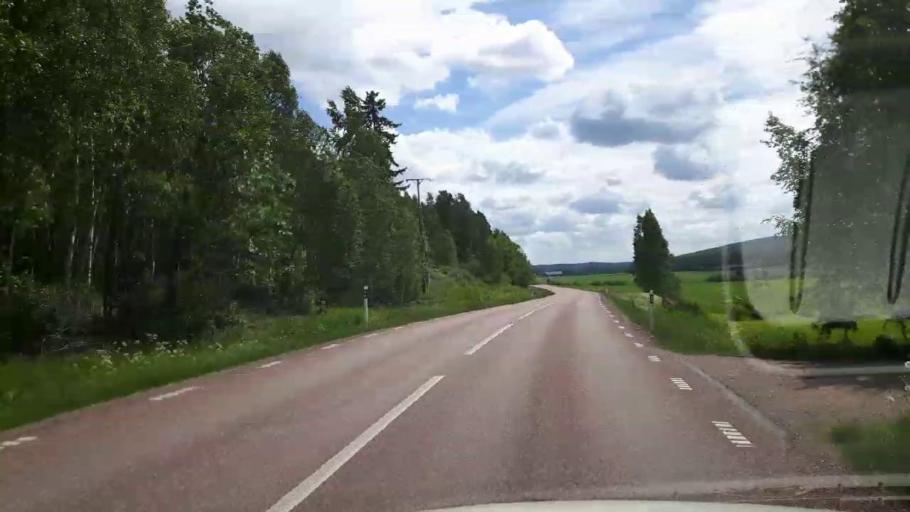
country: SE
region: Dalarna
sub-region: Saters Kommun
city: Saeter
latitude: 60.4105
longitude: 15.8586
